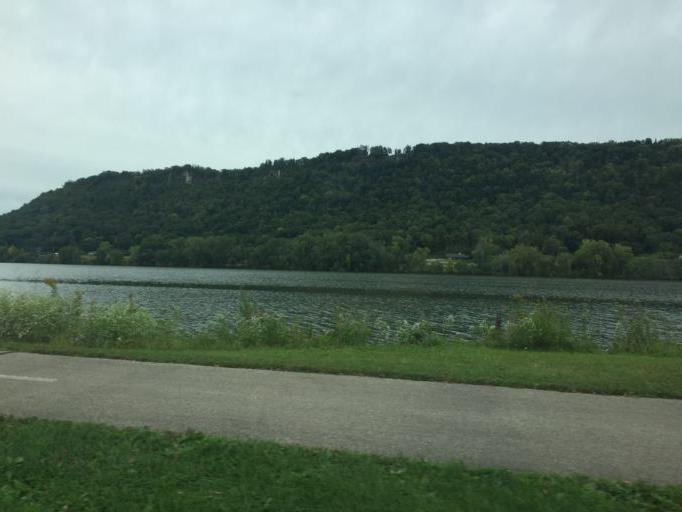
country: US
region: Minnesota
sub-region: Winona County
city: Winona
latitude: 44.0401
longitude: -91.6416
